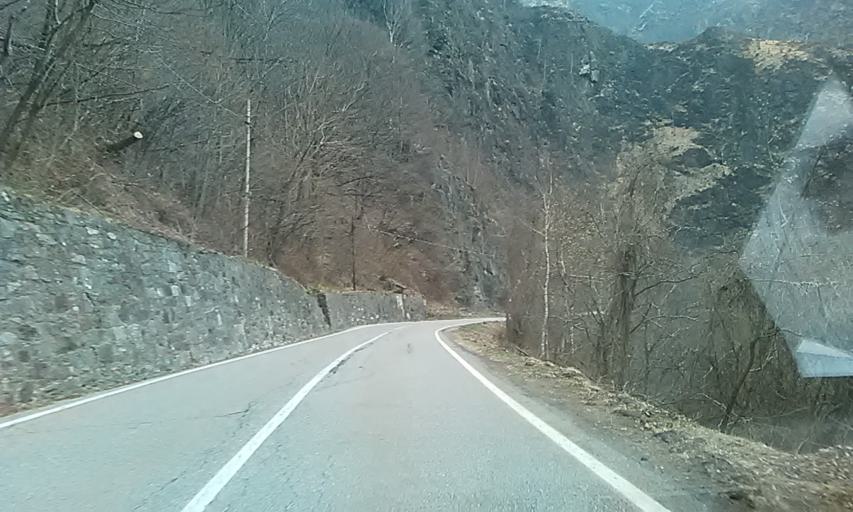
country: IT
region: Piedmont
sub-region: Provincia di Vercelli
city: Cervatto
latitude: 45.8808
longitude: 8.1744
